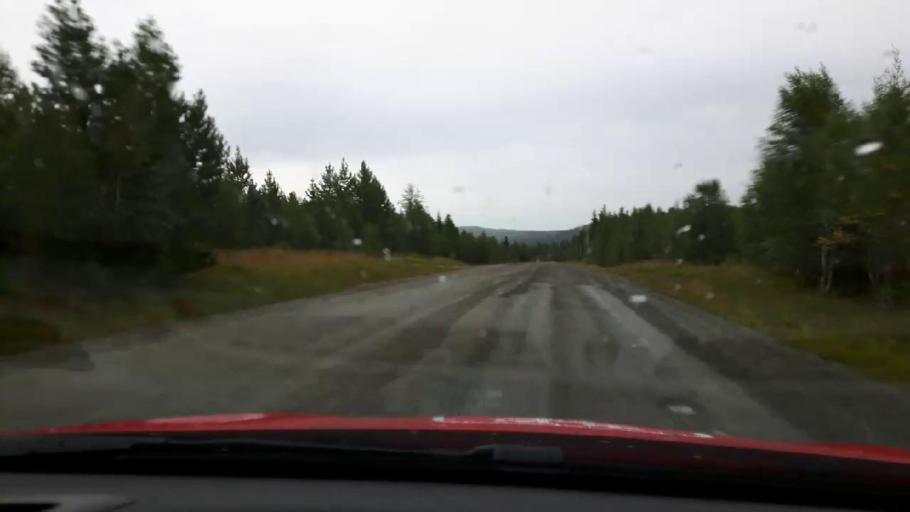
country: SE
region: Jaemtland
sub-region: Are Kommun
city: Are
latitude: 63.4095
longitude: 12.7957
